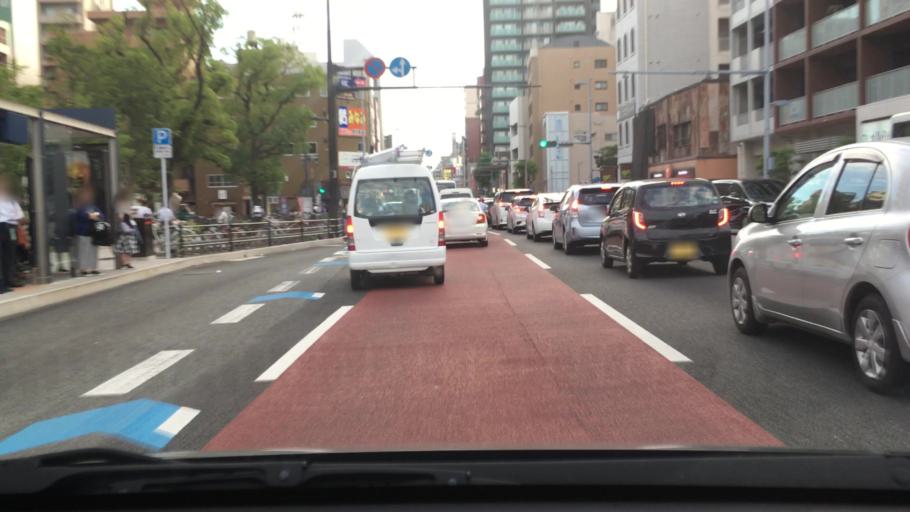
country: JP
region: Fukuoka
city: Fukuoka-shi
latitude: 33.5774
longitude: 130.3769
